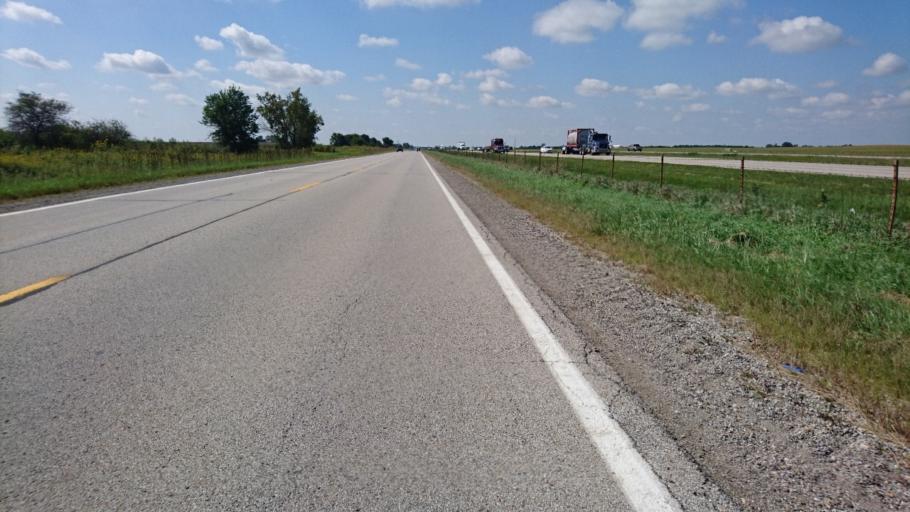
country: US
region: Illinois
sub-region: McLean County
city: Lexington
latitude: 40.6159
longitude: -88.8228
